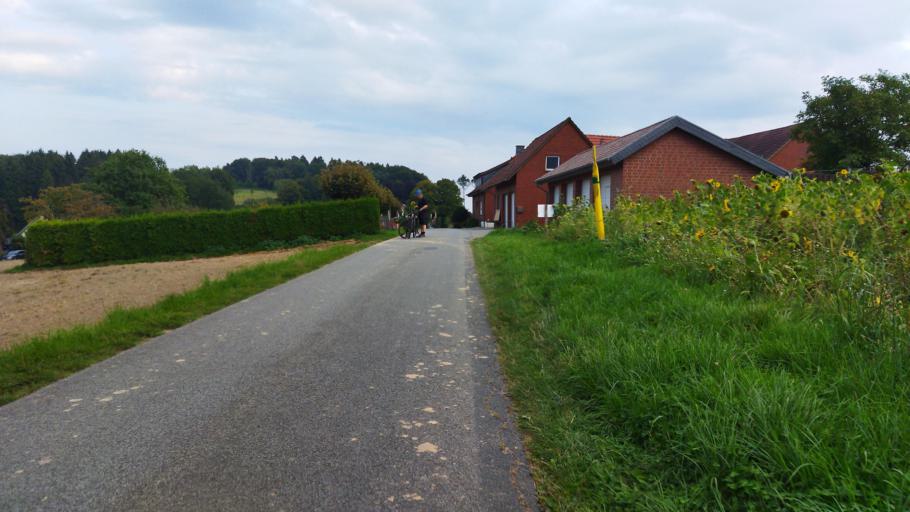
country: DE
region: Lower Saxony
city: Bad Iburg
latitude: 52.1737
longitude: 8.0147
